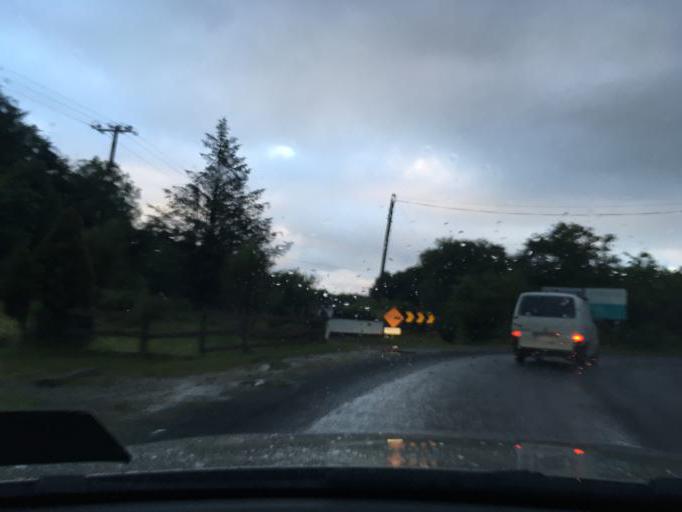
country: IE
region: Ulster
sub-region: County Donegal
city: Killybegs
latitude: 54.6362
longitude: -8.4675
